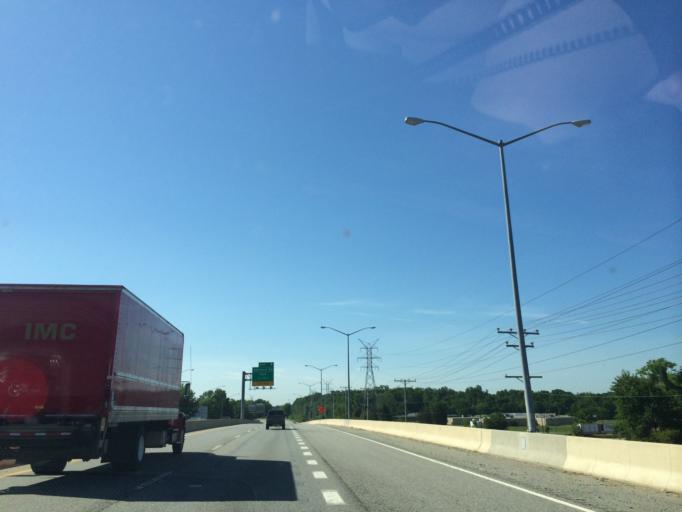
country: US
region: Maryland
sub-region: Howard County
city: Fort George G Mead Junction
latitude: 39.1092
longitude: -76.7750
